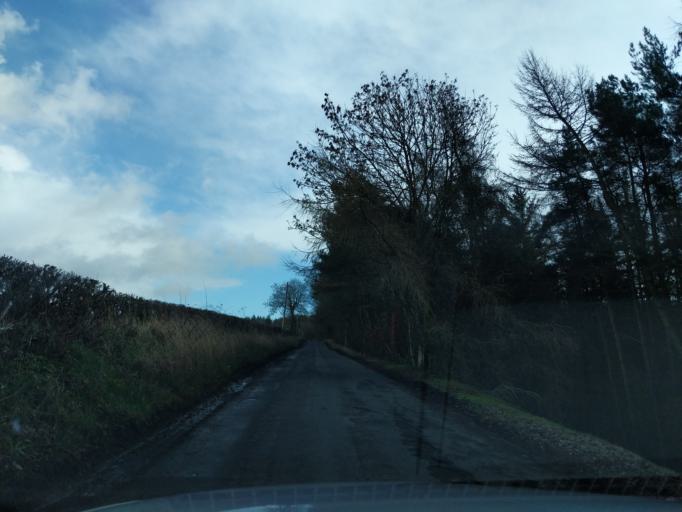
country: GB
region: Scotland
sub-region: Edinburgh
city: Balerno
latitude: 55.8757
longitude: -3.3217
